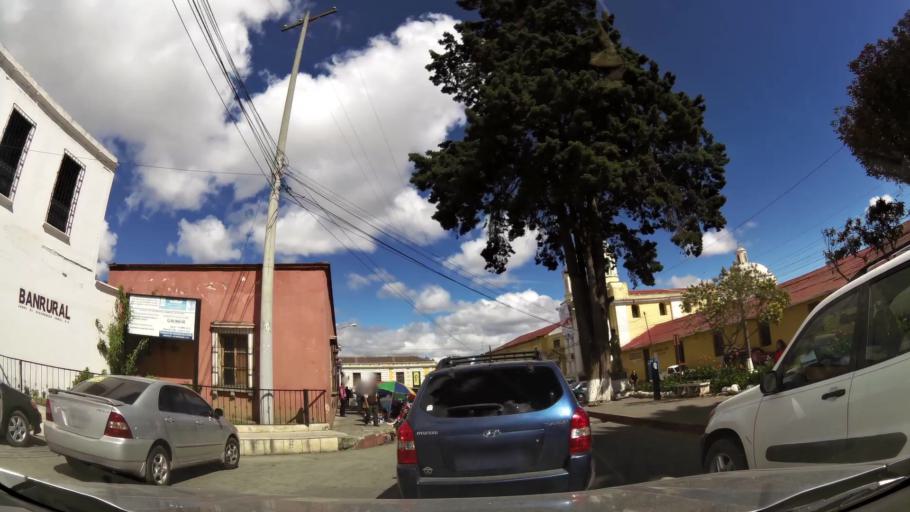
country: GT
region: Quetzaltenango
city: Quetzaltenango
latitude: 14.8393
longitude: -91.5182
